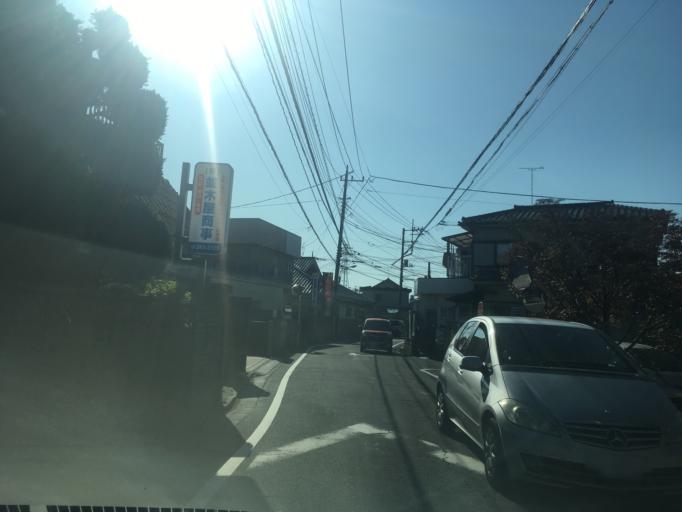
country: JP
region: Saitama
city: Kawagoe
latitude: 35.9057
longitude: 139.4698
